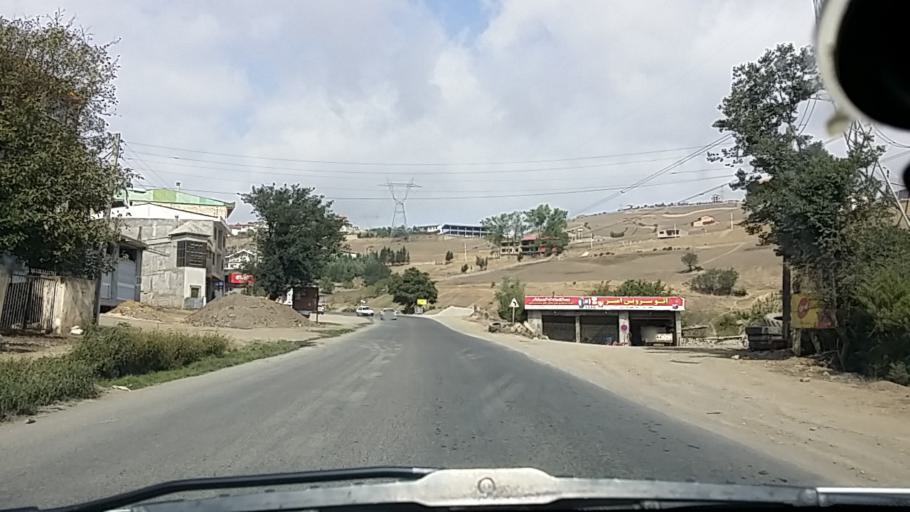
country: IR
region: Mazandaran
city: Chalus
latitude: 36.4958
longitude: 51.2636
